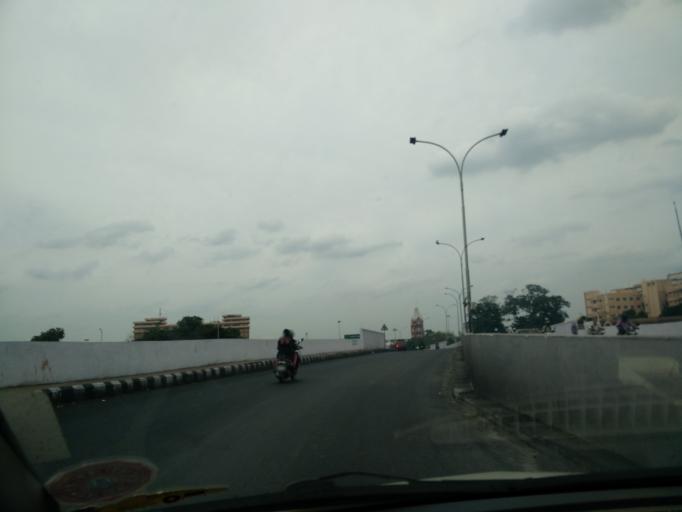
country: IN
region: Tamil Nadu
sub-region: Chennai
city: Chennai
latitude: 13.0788
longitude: 80.2751
